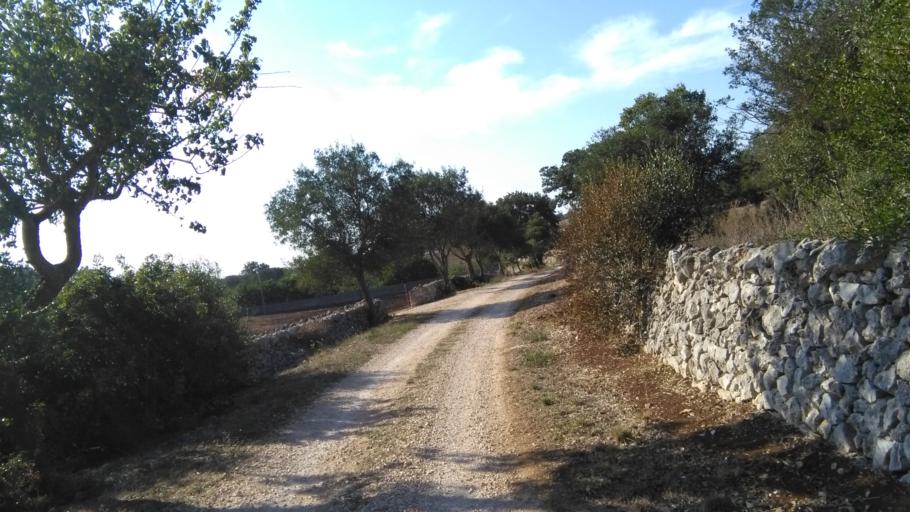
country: IT
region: Apulia
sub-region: Provincia di Bari
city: Putignano
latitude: 40.8208
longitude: 17.0577
